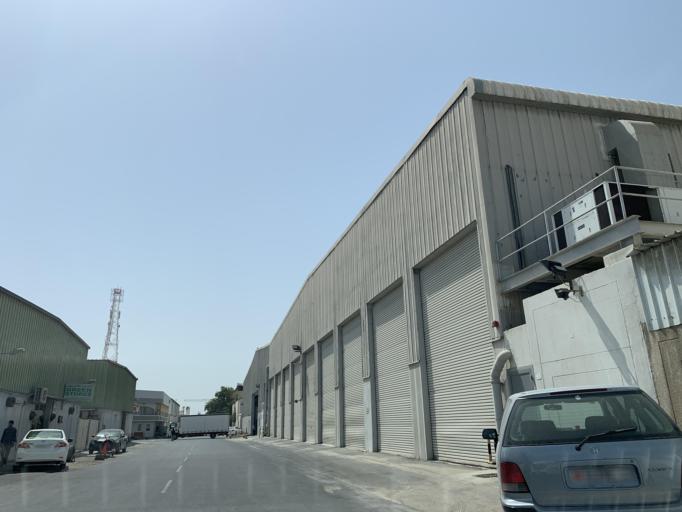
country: BH
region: Northern
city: Madinat `Isa
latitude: 26.1923
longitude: 50.5386
